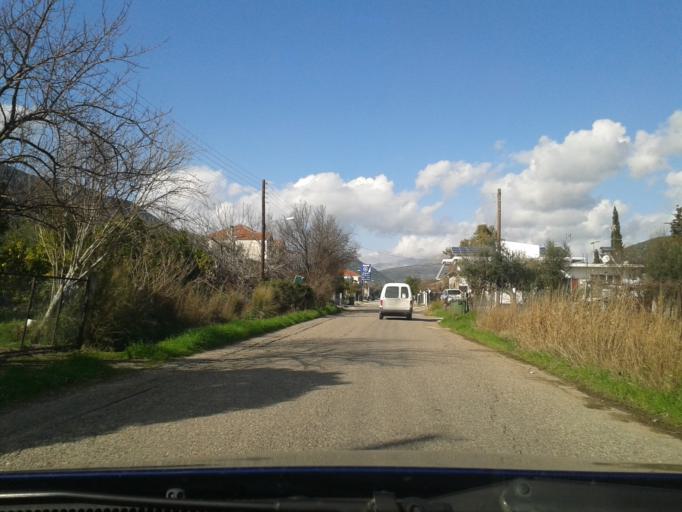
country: GR
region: West Greece
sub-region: Nomos Aitolias kai Akarnanias
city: Astakos
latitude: 38.5715
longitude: 21.0943
